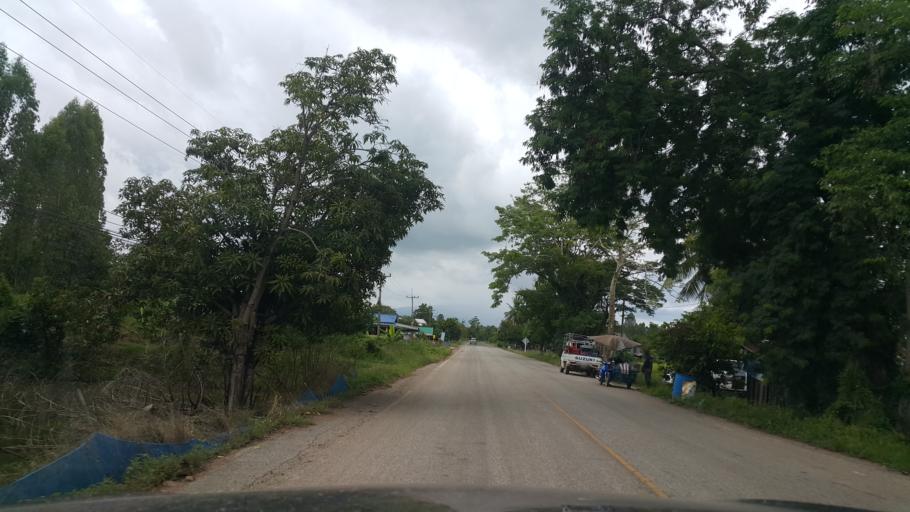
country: TH
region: Sukhothai
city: Sukhothai
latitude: 16.9167
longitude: 99.8721
